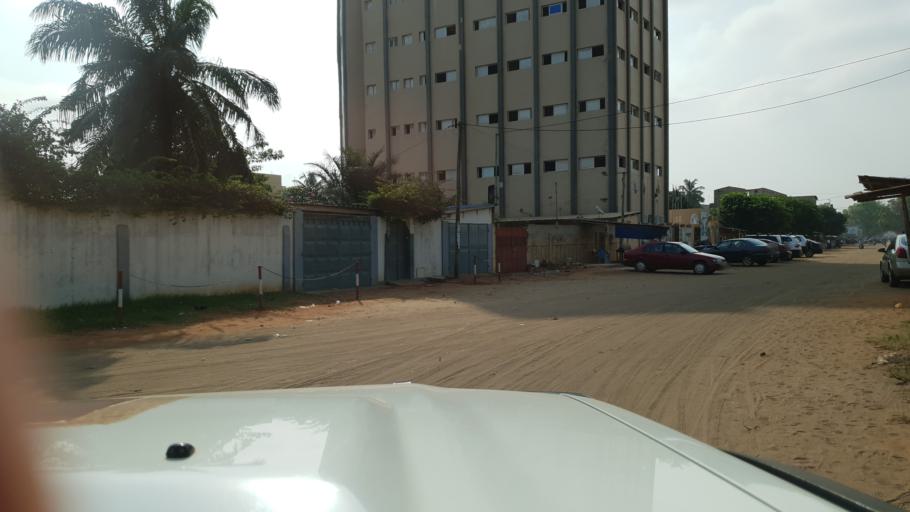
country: TG
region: Maritime
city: Lome
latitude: 6.1651
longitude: 1.2141
